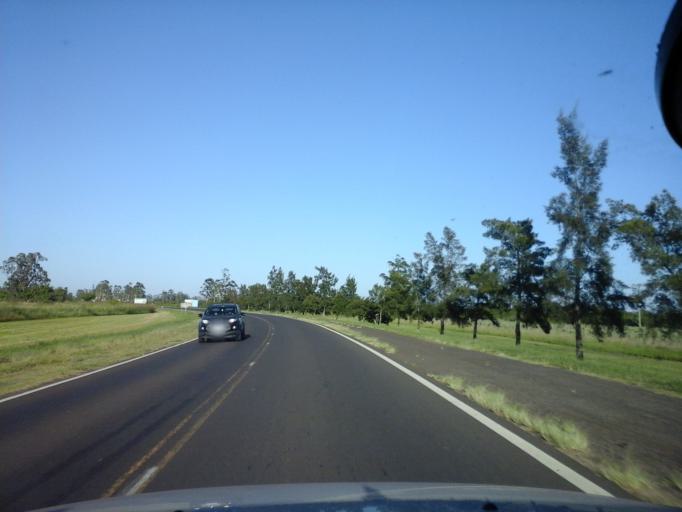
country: AR
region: Corrientes
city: Ita Ibate
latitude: -27.4393
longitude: -57.3455
